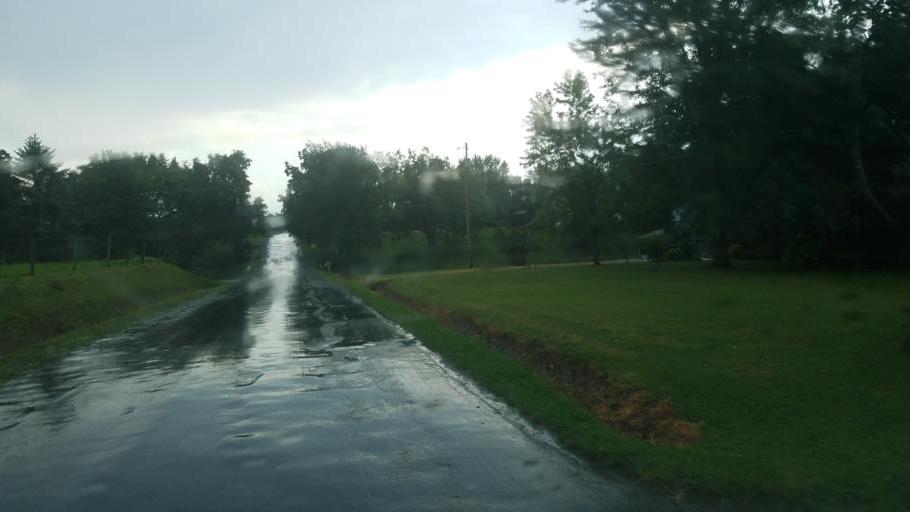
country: US
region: Ohio
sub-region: Geauga County
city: Middlefield
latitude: 41.4647
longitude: -80.9748
